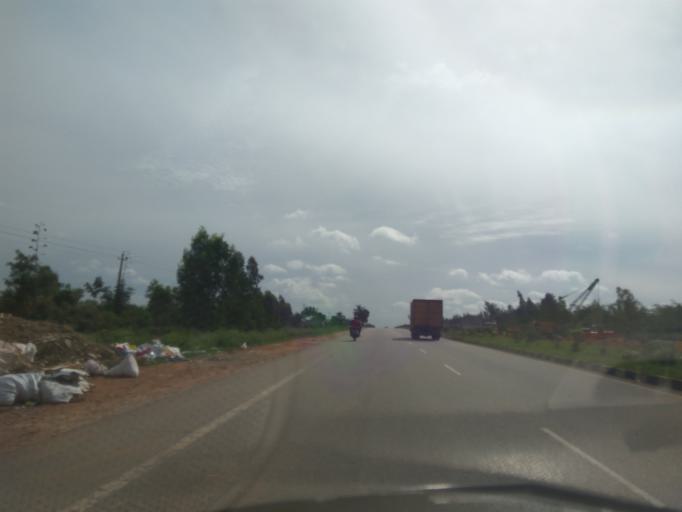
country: IN
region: Karnataka
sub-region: Bangalore Rural
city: Dasarahalli
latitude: 13.0951
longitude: 77.8473
